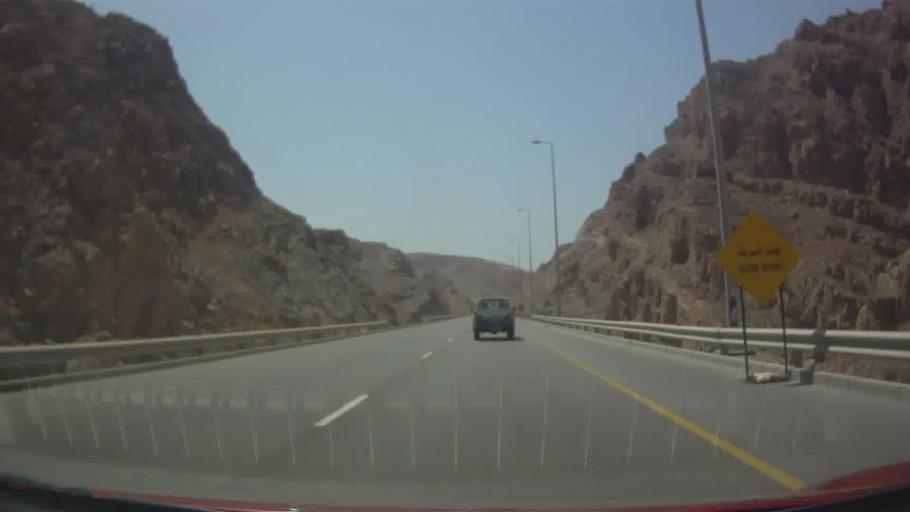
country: OM
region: Muhafazat Masqat
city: Muscat
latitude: 23.5277
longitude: 58.6444
